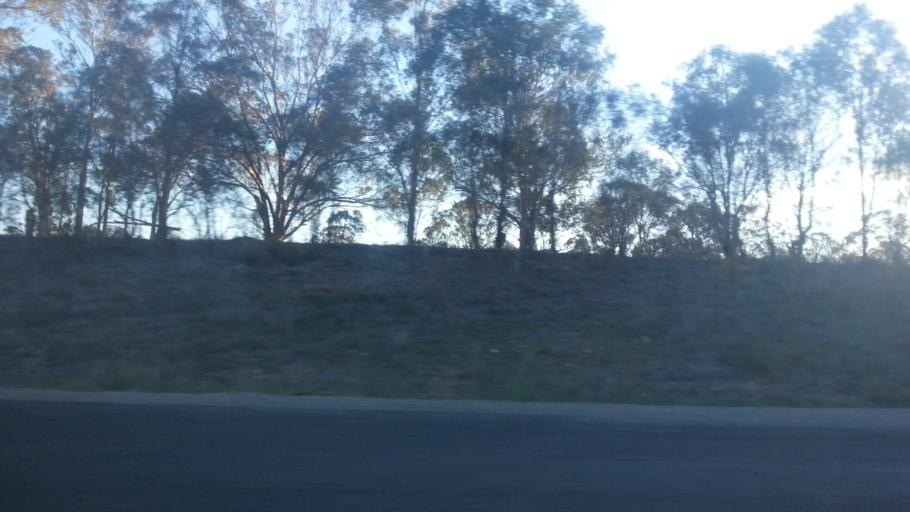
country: AU
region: New South Wales
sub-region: Wollondilly
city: Douglas Park
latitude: -34.2018
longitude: 150.7103
